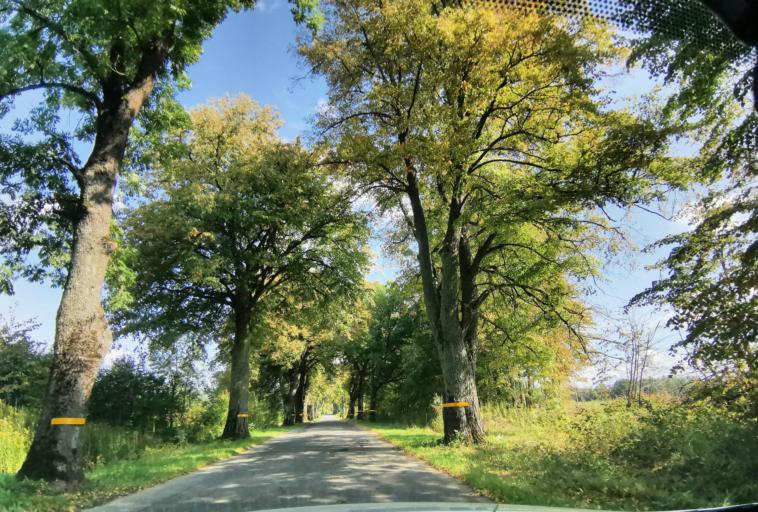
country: RU
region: Kaliningrad
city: Chernyakhovsk
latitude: 54.6598
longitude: 21.9193
